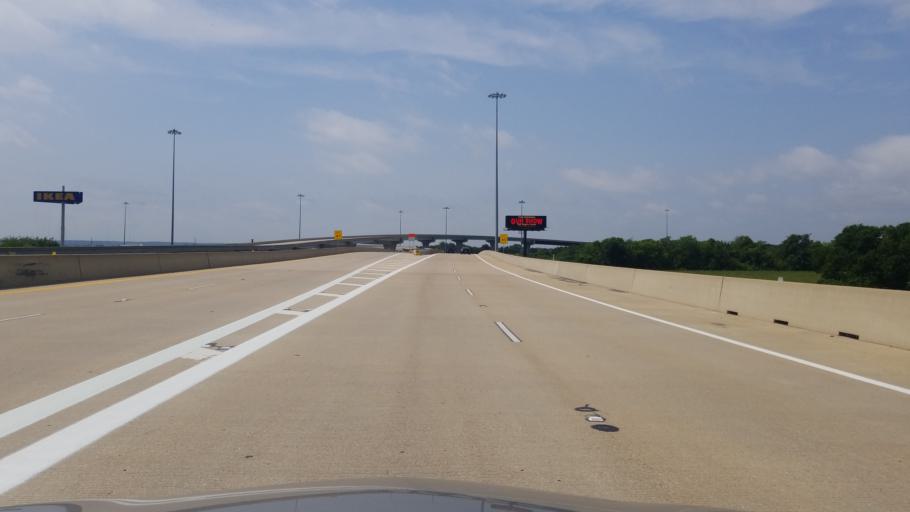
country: US
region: Texas
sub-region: Dallas County
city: Grand Prairie
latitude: 32.6810
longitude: -97.0240
